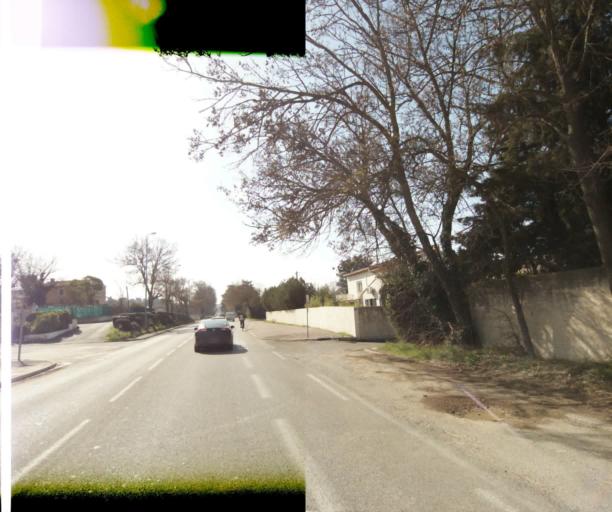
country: FR
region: Provence-Alpes-Cote d'Azur
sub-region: Departement des Bouches-du-Rhone
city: Bouc-Bel-Air
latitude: 43.4584
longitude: 5.4043
